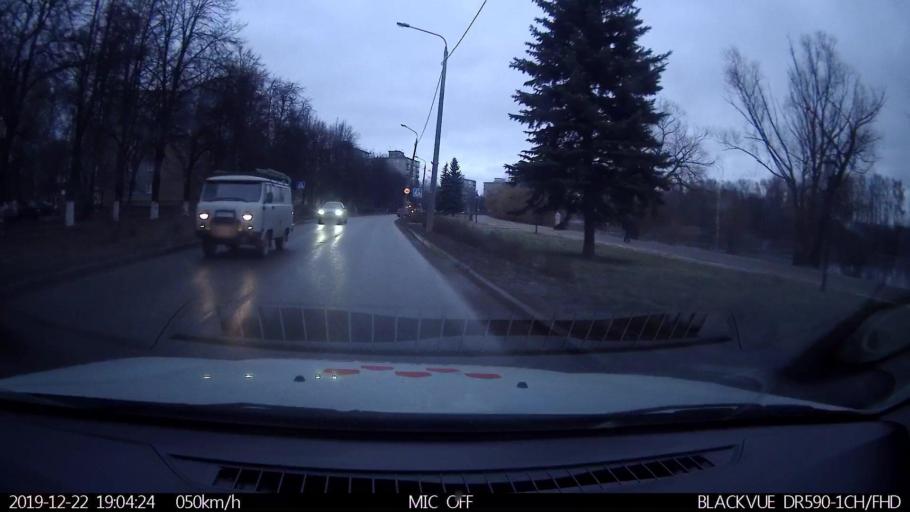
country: RU
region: Nizjnij Novgorod
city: Gorbatovka
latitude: 56.3414
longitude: 43.8482
